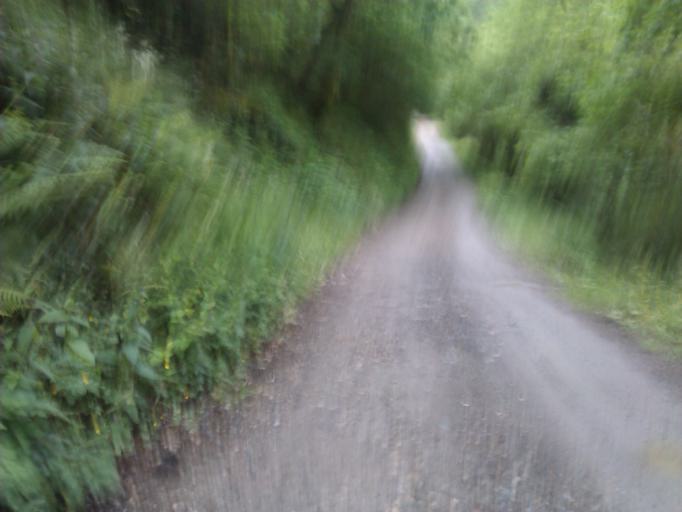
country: ES
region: Basque Country
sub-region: Provincia de Guipuzcoa
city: Elduayen
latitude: 43.1755
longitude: -1.9849
